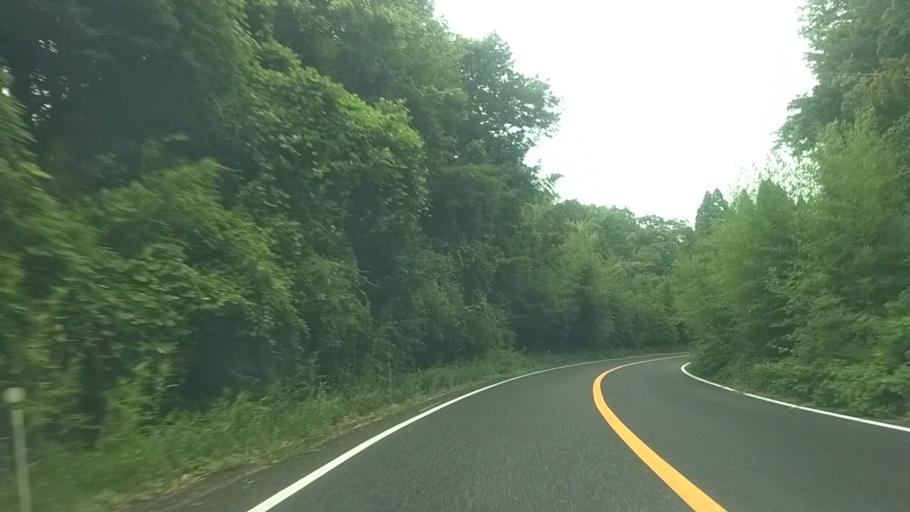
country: JP
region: Chiba
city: Kimitsu
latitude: 35.2440
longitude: 140.0055
